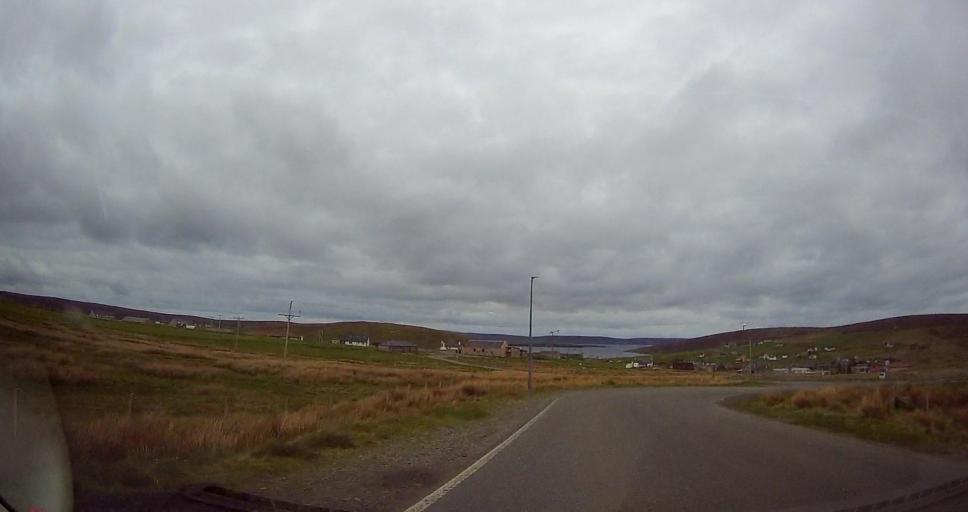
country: GB
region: Scotland
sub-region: Shetland Islands
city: Shetland
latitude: 60.5992
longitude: -1.0745
